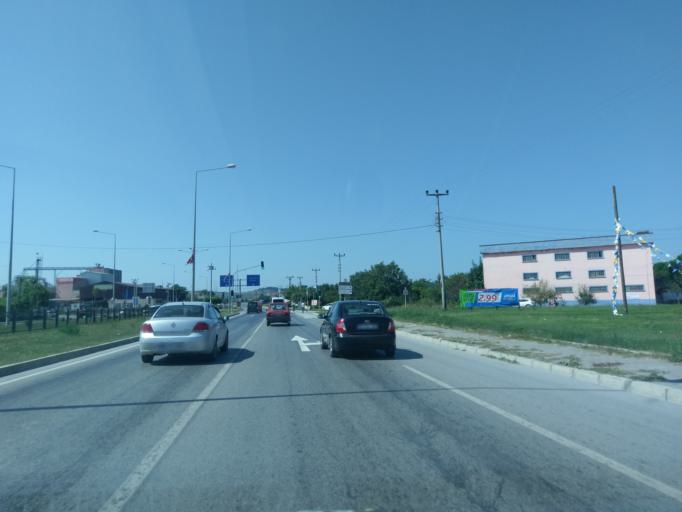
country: TR
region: Samsun
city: Bafra
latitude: 41.5697
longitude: 35.8761
